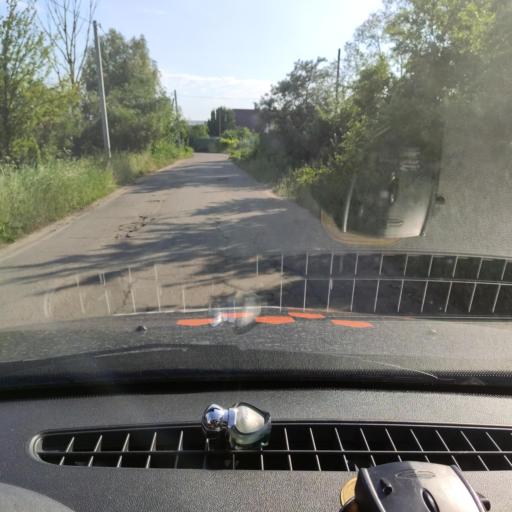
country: RU
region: Voronezj
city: Podkletnoye
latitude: 51.6201
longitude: 39.4475
